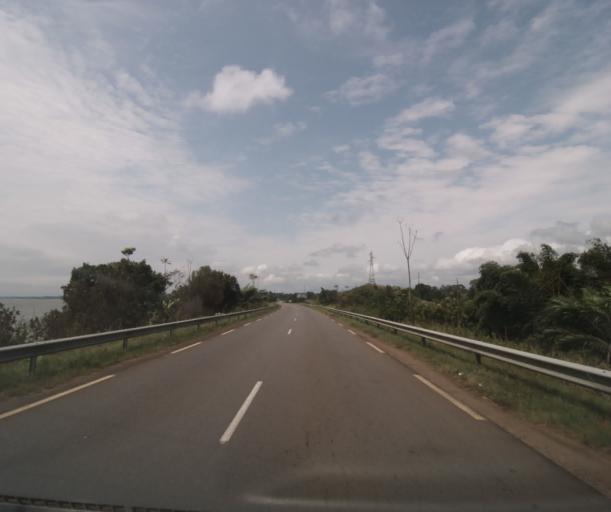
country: CM
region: South Province
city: Kribi
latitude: 3.0074
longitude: 9.9484
